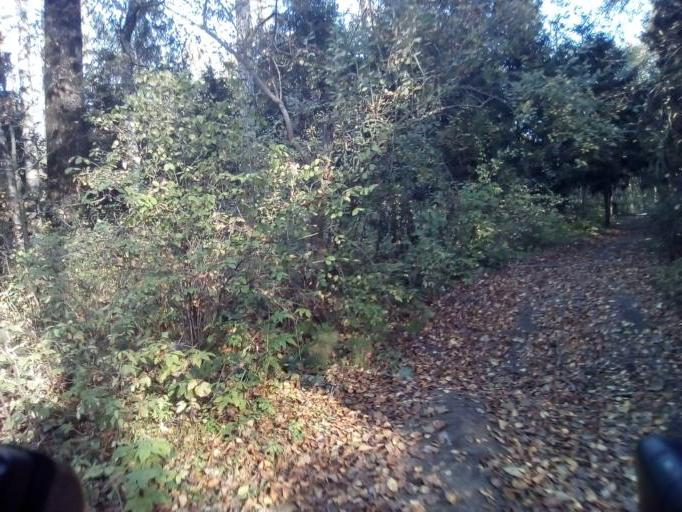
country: RU
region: Moskovskaya
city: Ramenskoye
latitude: 55.5748
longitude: 38.3110
